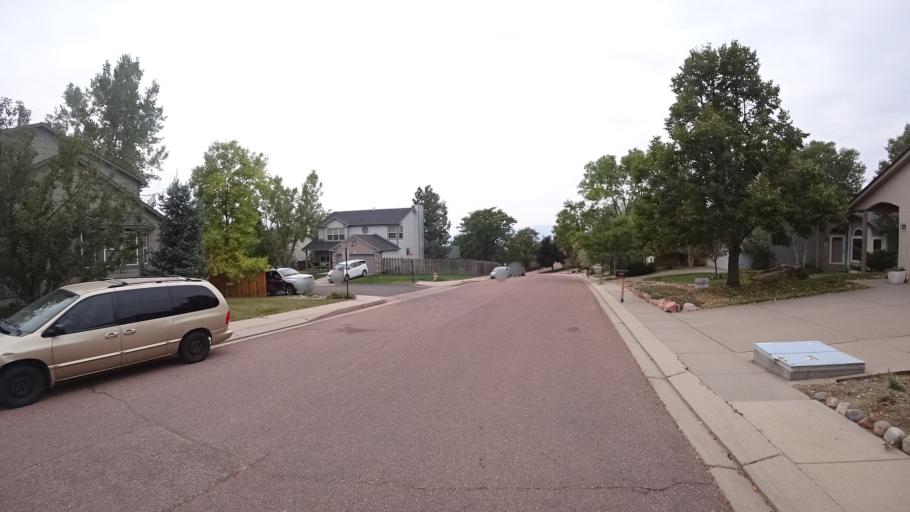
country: US
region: Colorado
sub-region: El Paso County
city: Cimarron Hills
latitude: 38.9089
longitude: -104.7322
